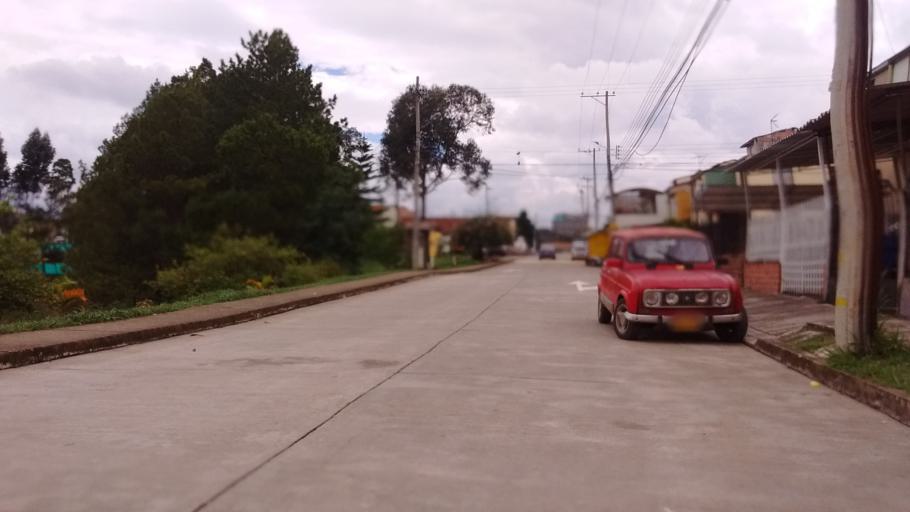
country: CO
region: Cauca
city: Popayan
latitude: 2.4807
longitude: -76.5798
